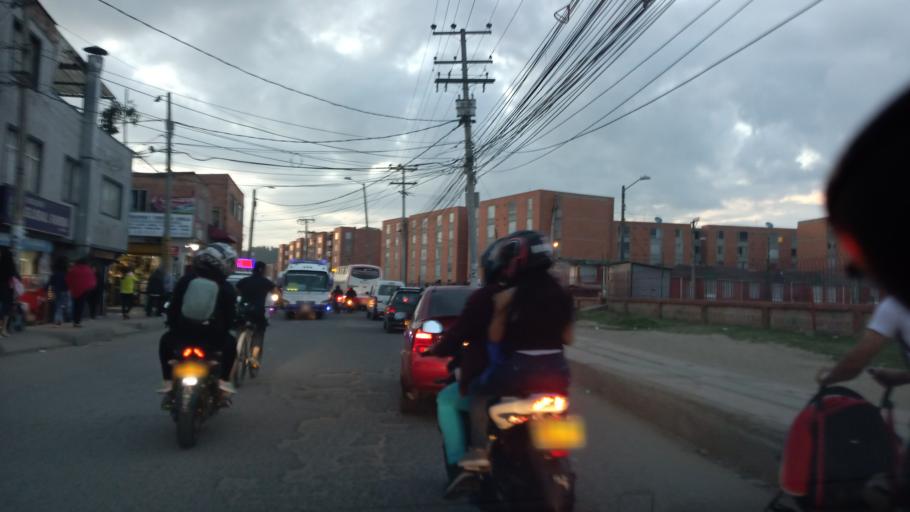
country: CO
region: Cundinamarca
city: Soacha
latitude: 4.5824
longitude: -74.2239
